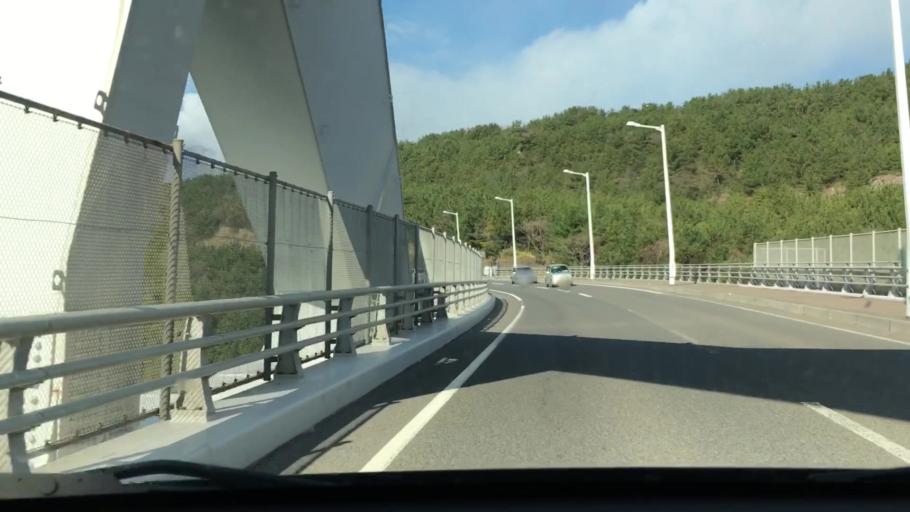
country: JP
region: Kagoshima
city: Tarumizu
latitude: 31.5594
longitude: 130.7161
